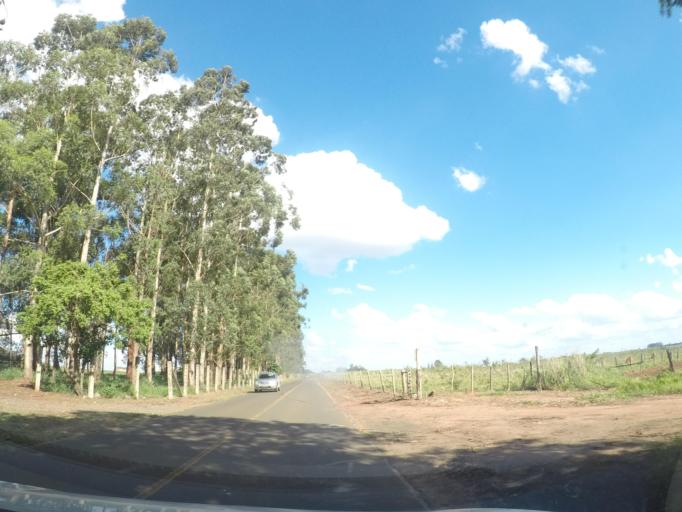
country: BR
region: Sao Paulo
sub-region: Sumare
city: Sumare
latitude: -22.8532
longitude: -47.3242
